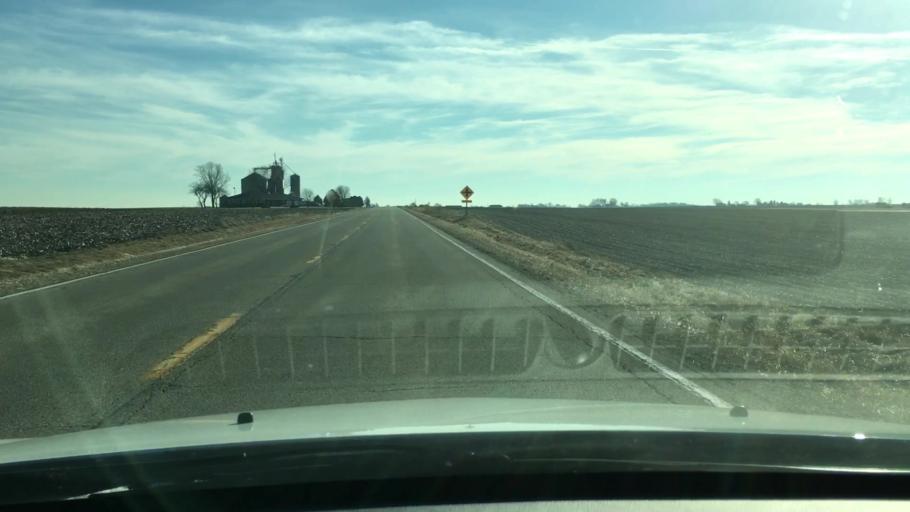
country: US
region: Illinois
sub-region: LaSalle County
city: Mendota
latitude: 41.5008
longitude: -89.1271
